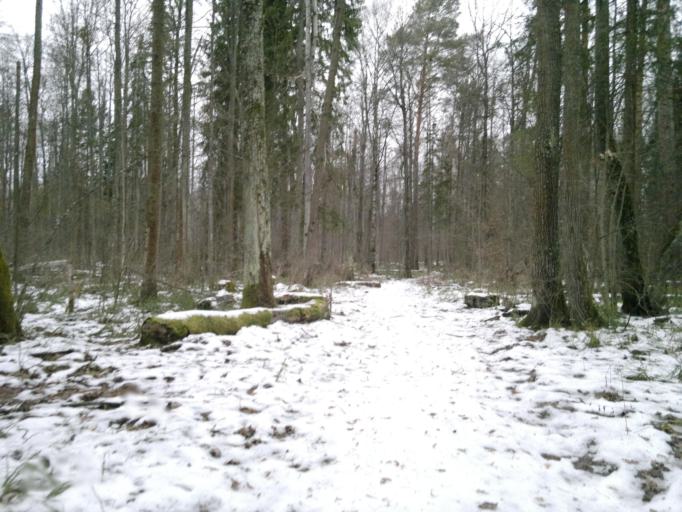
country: RU
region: Mariy-El
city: Yoshkar-Ola
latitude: 56.6127
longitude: 47.9468
